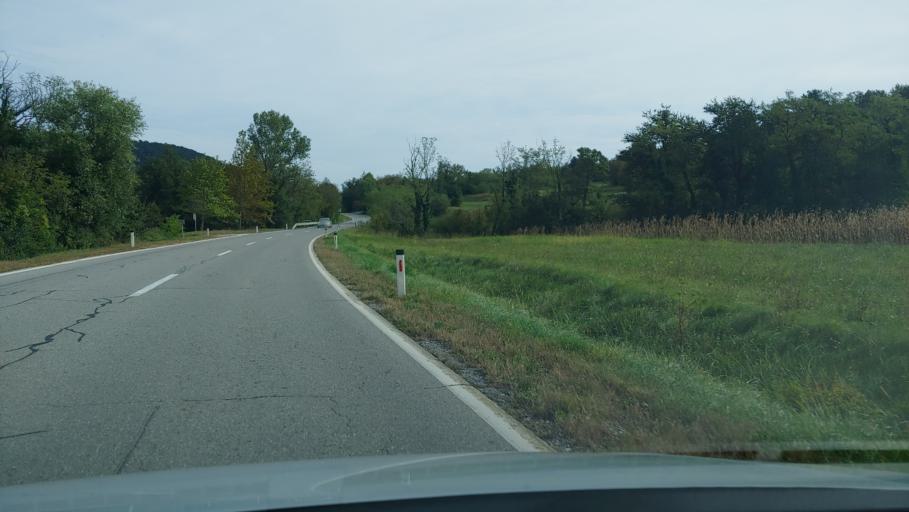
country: SI
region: Nova Gorica
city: Sempas
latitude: 45.9176
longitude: 13.7618
